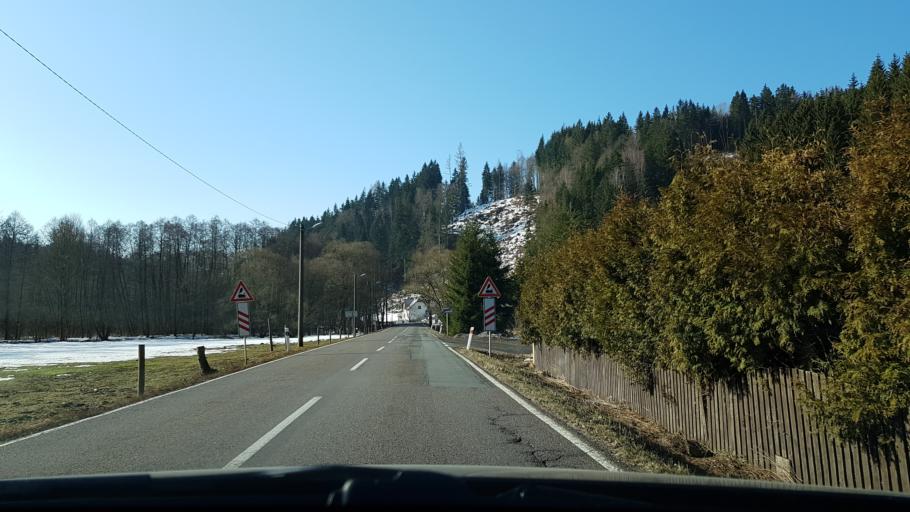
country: CZ
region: Olomoucky
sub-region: Okres Sumperk
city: Hanusovice
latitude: 50.0936
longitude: 16.9774
